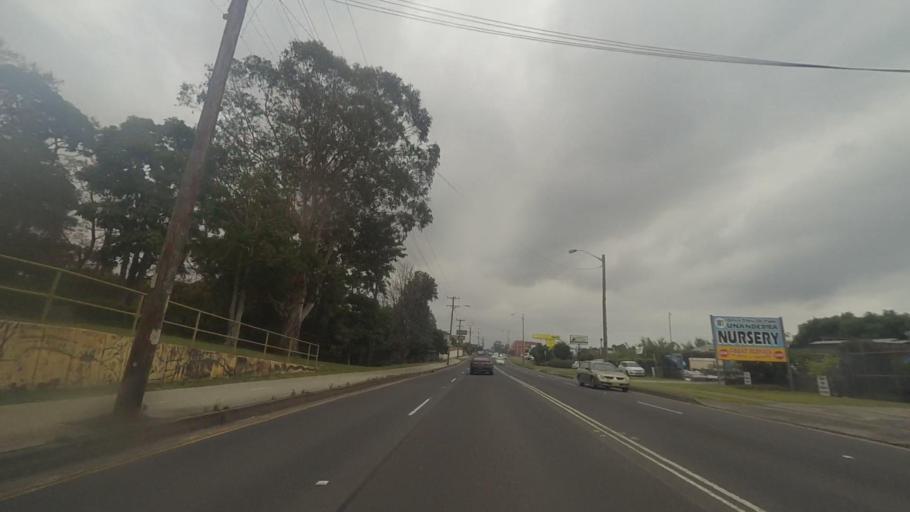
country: AU
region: New South Wales
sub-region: Wollongong
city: Cordeaux Heights
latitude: -34.4572
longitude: 150.8426
